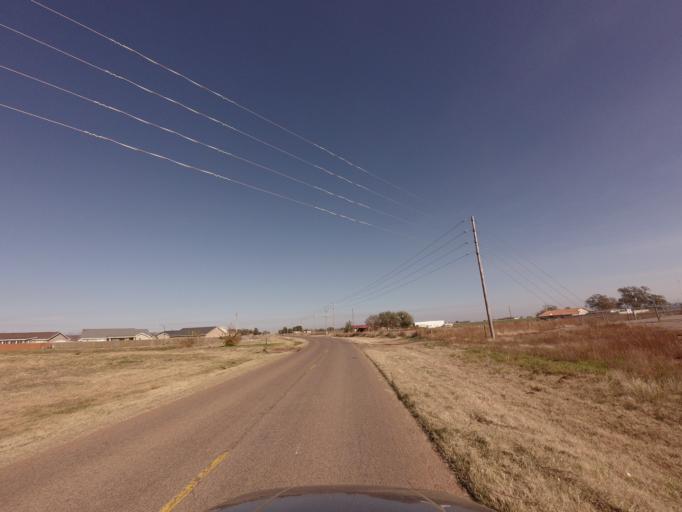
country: US
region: New Mexico
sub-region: Curry County
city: Clovis
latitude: 34.4119
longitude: -103.1608
